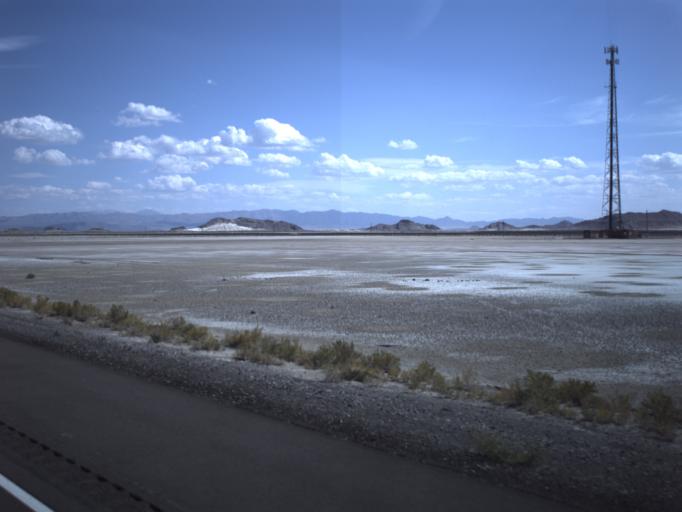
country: US
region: Utah
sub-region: Tooele County
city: Wendover
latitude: 40.7276
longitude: -113.3350
